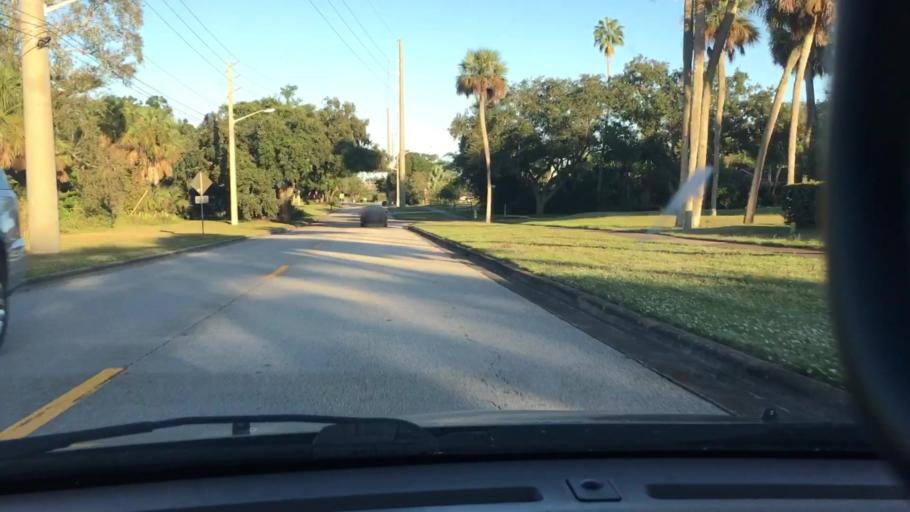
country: US
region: Florida
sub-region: Indian River County
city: Vero Beach
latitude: 27.6456
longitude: -80.4030
